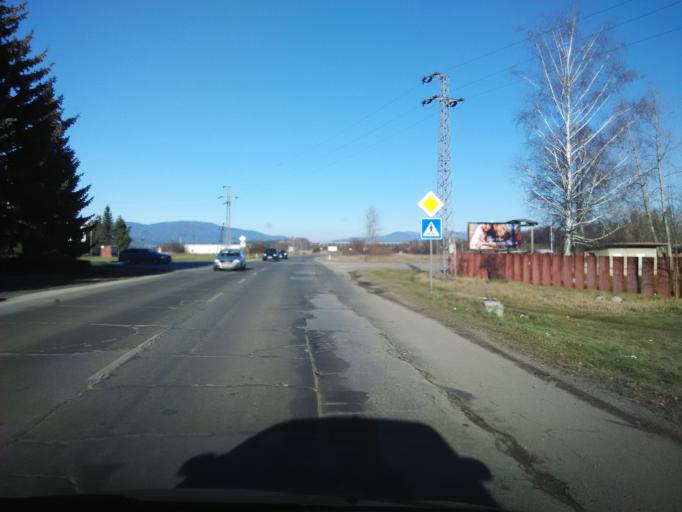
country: SK
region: Nitriansky
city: Handlova
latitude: 48.8815
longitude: 18.8566
